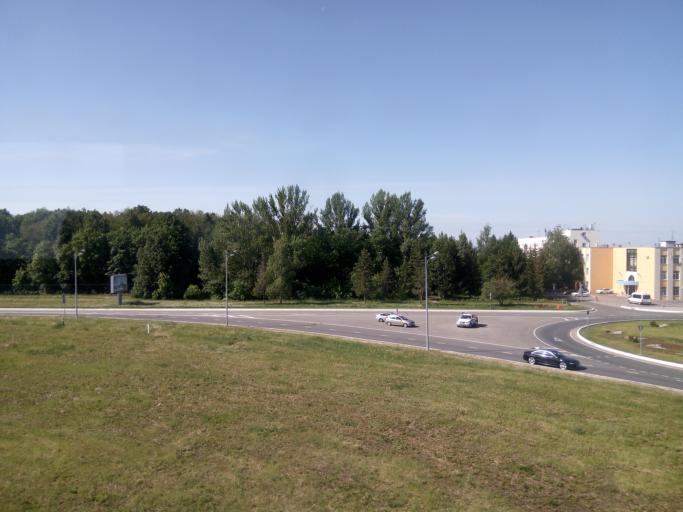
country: RU
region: Tatarstan
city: Stolbishchi
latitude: 55.6143
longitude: 49.2865
